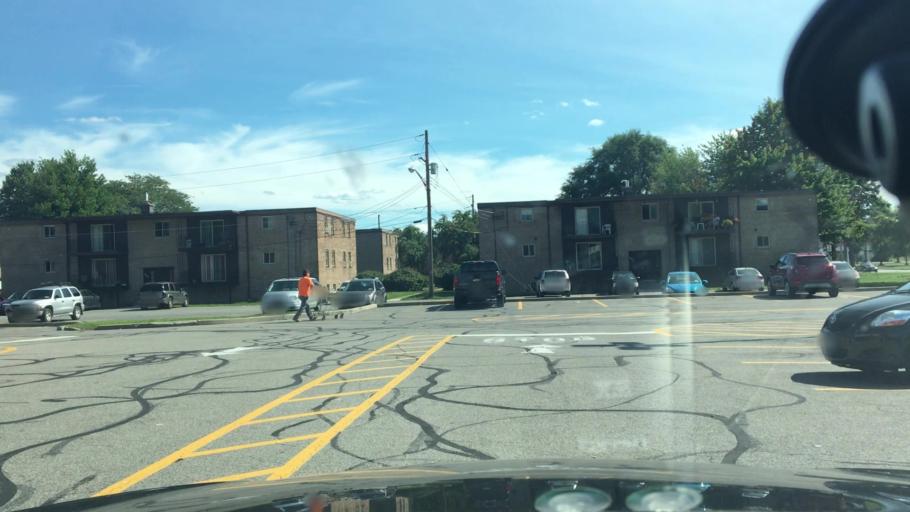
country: US
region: New York
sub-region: Erie County
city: West Seneca
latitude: 42.8665
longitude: -78.7866
